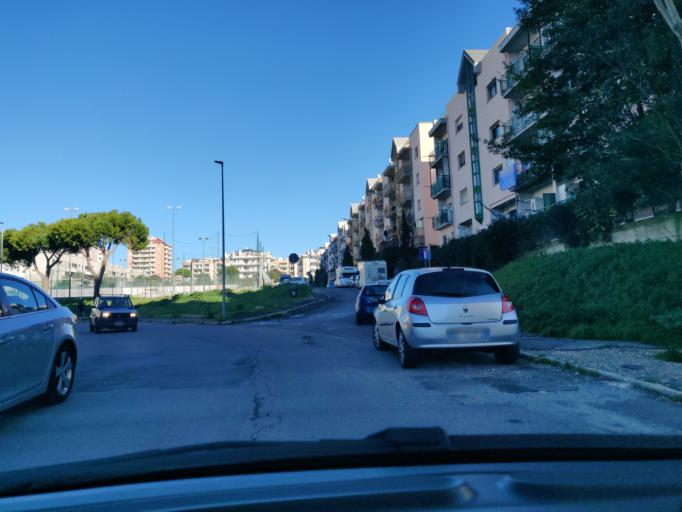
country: IT
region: Latium
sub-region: Citta metropolitana di Roma Capitale
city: Civitavecchia
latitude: 42.0967
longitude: 11.8225
